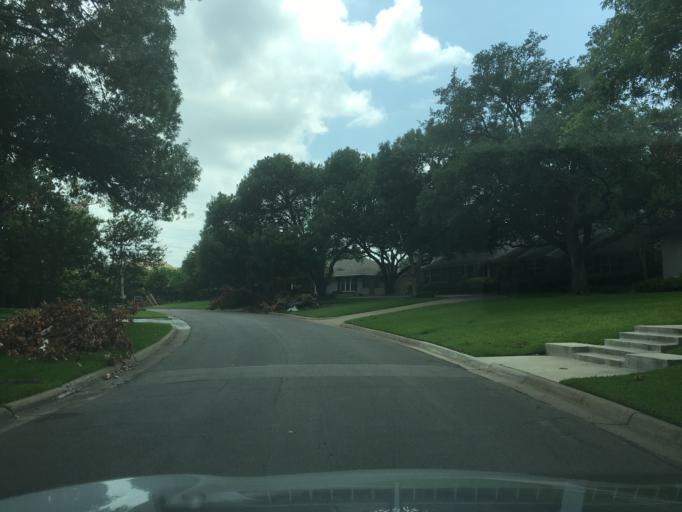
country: US
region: Texas
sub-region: Dallas County
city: Addison
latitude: 32.9039
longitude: -96.8241
